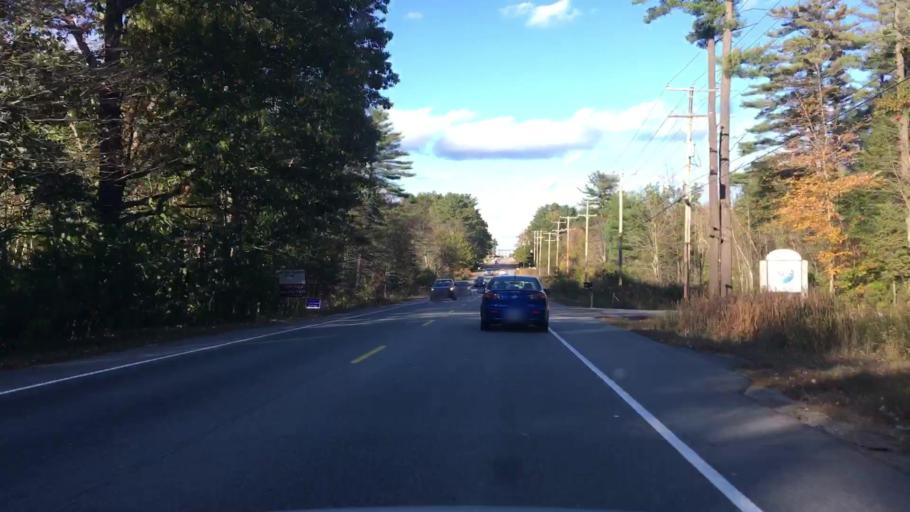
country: US
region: Maine
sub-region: Cumberland County
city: South Portland Gardens
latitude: 43.6150
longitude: -70.3561
